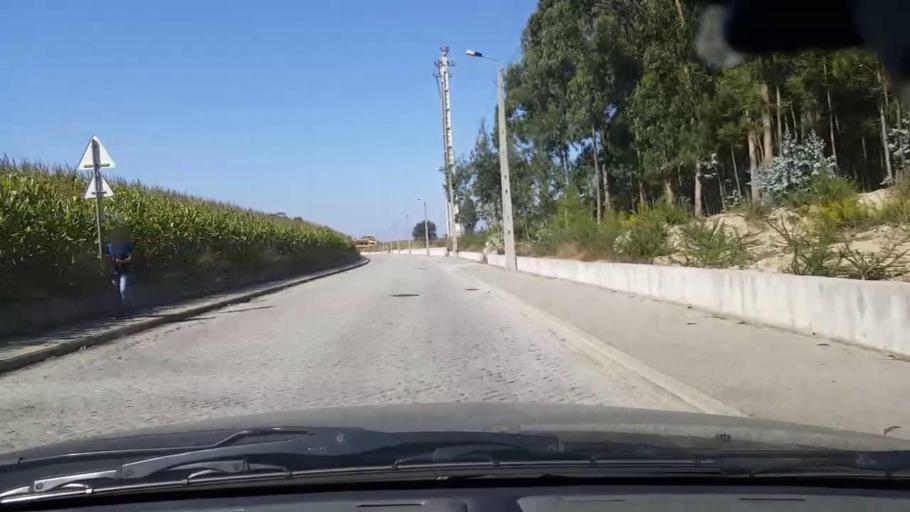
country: PT
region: Porto
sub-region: Vila do Conde
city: Arvore
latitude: 41.3017
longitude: -8.7118
